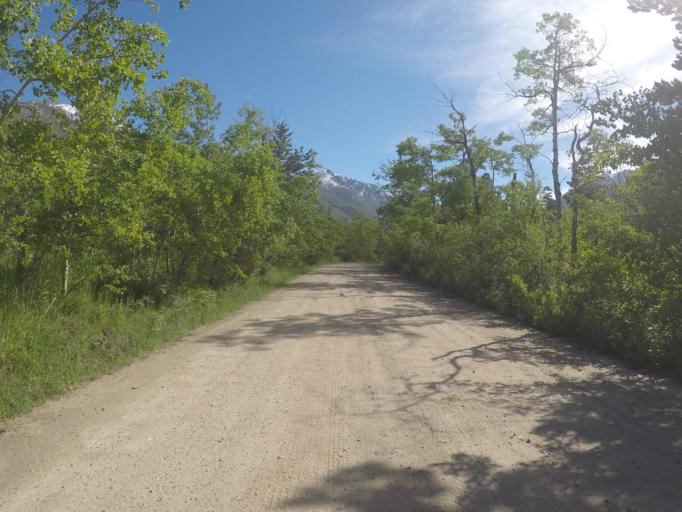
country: US
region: Montana
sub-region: Stillwater County
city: Absarokee
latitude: 45.2640
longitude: -109.5626
